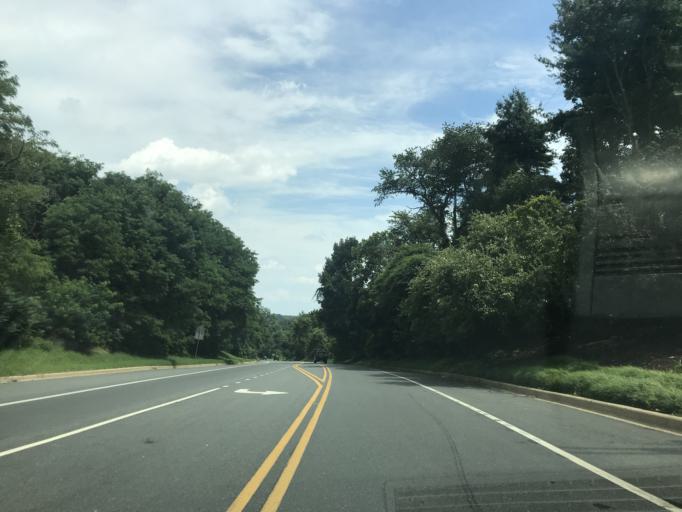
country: US
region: Delaware
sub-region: New Castle County
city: Hockessin
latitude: 39.7652
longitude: -75.6524
